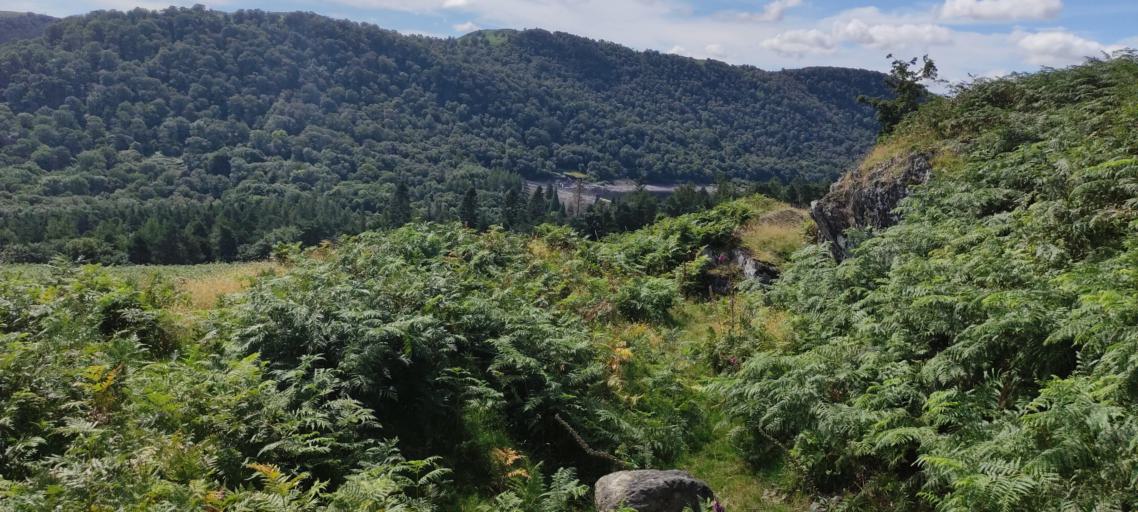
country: GB
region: England
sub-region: Cumbria
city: Penrith
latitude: 54.5398
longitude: -2.7670
